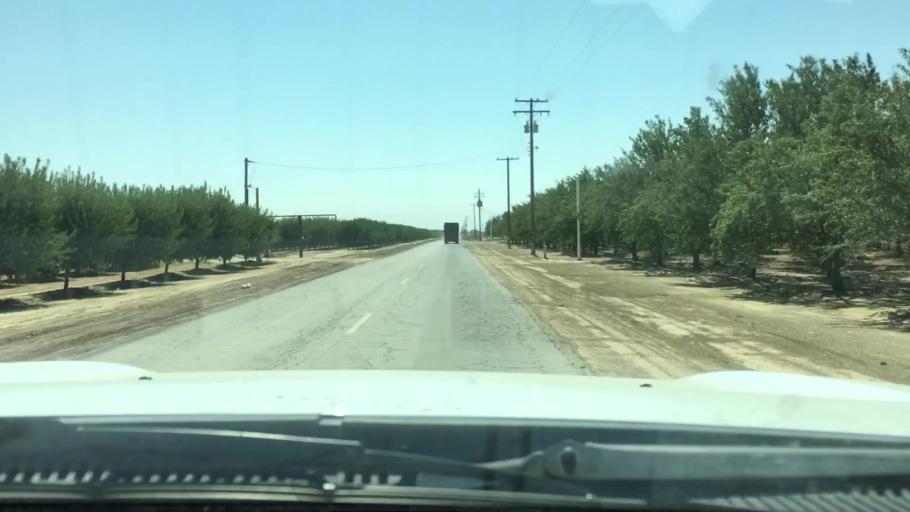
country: US
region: California
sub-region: Kern County
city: Wasco
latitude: 35.5189
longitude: -119.4033
